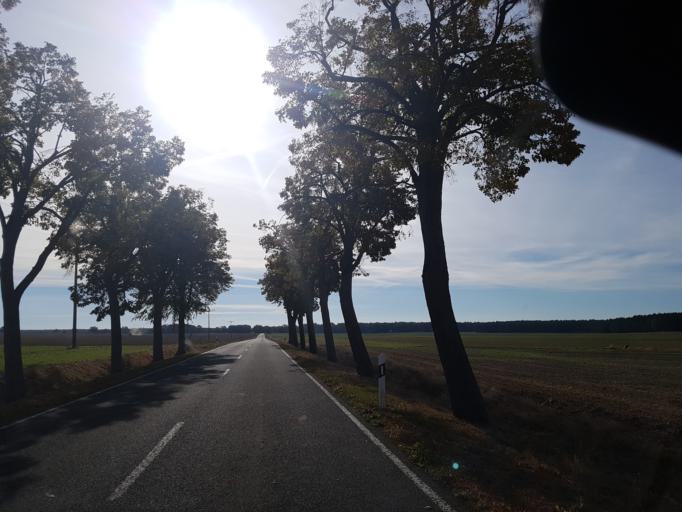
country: DE
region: Brandenburg
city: Ihlow
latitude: 51.8956
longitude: 13.2323
